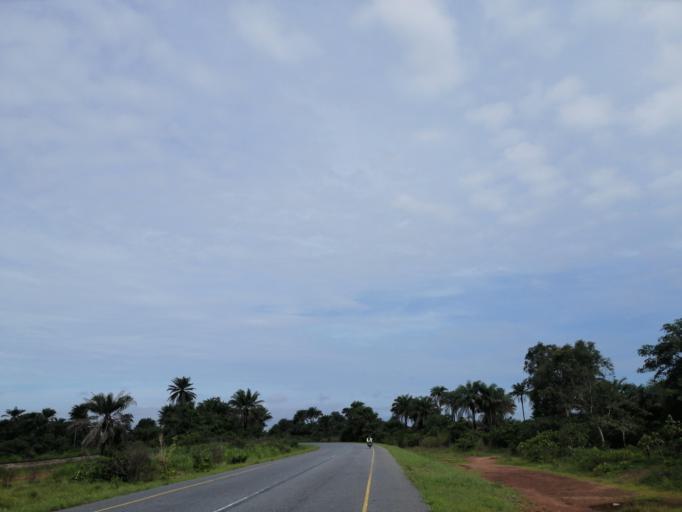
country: SL
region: Northern Province
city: Port Loko
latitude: 8.7701
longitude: -12.8796
